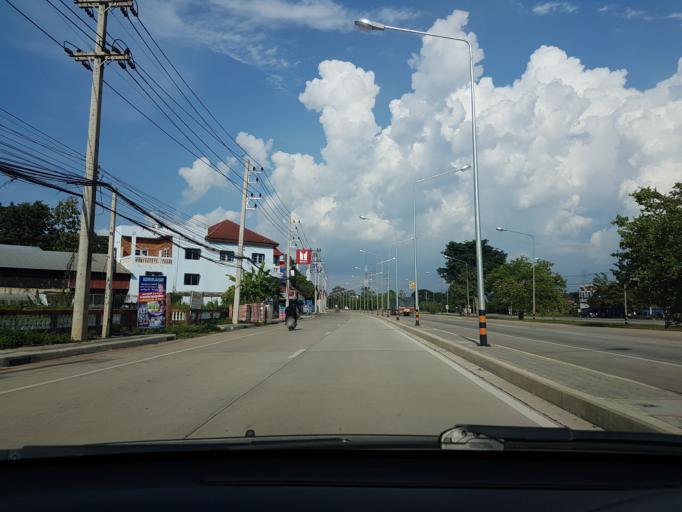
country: TH
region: Lampang
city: Lampang
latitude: 18.2456
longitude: 99.4480
